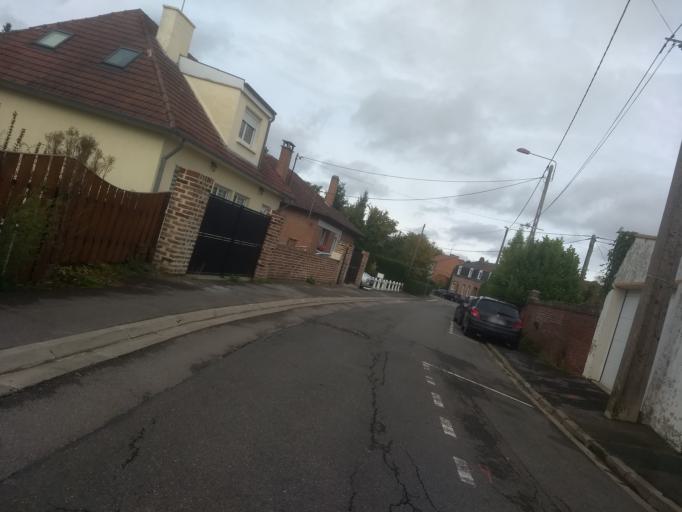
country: FR
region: Nord-Pas-de-Calais
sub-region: Departement du Pas-de-Calais
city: Anzin-Saint-Aubin
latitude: 50.3083
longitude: 2.7533
